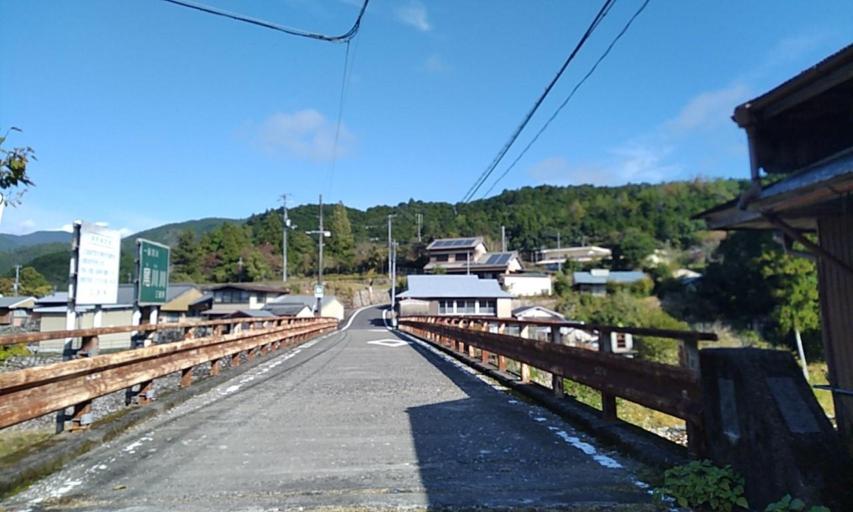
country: JP
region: Wakayama
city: Shingu
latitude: 33.9227
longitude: 135.9831
